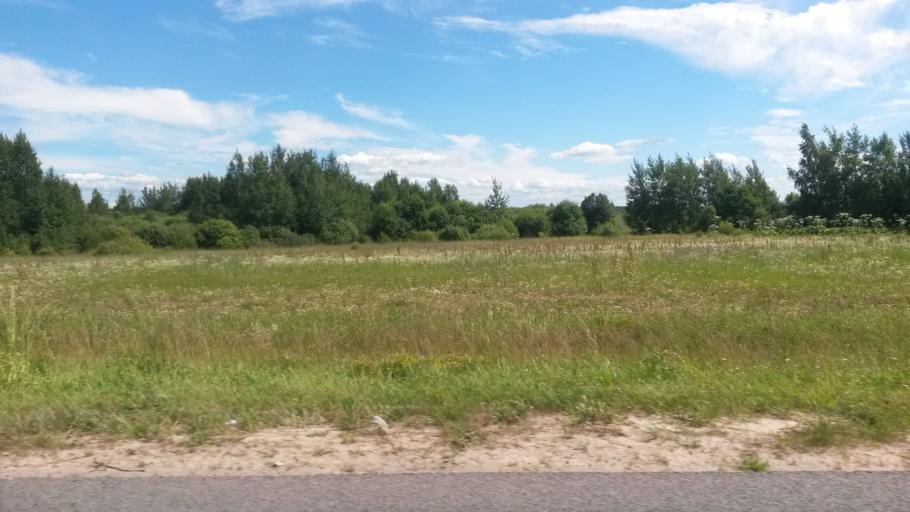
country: RU
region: Ivanovo
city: Staraya Vichuga
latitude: 57.2417
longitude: 41.8896
